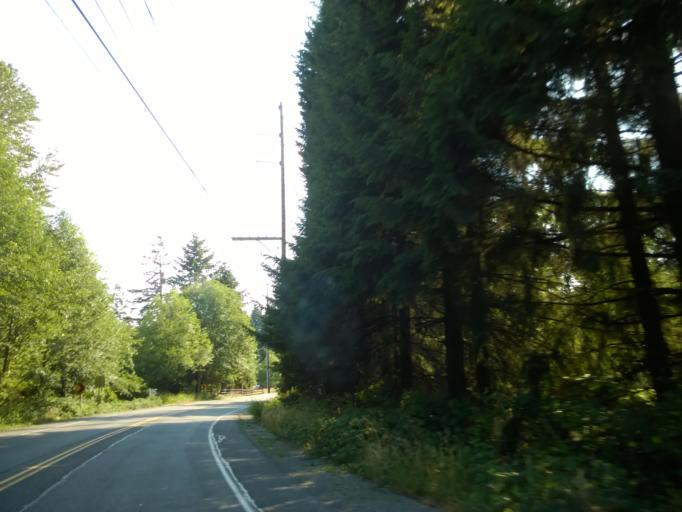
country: US
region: Washington
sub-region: King County
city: Union Hill-Novelty Hill
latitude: 47.6895
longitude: -122.0597
